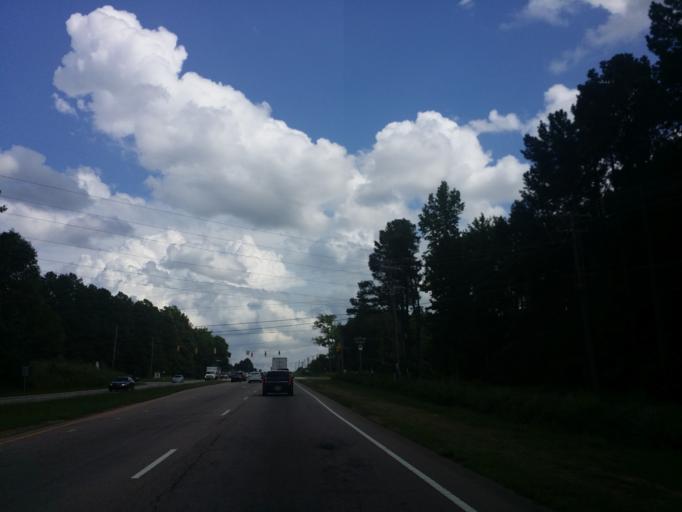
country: US
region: North Carolina
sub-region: Durham County
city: Gorman
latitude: 35.9359
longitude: -78.8147
